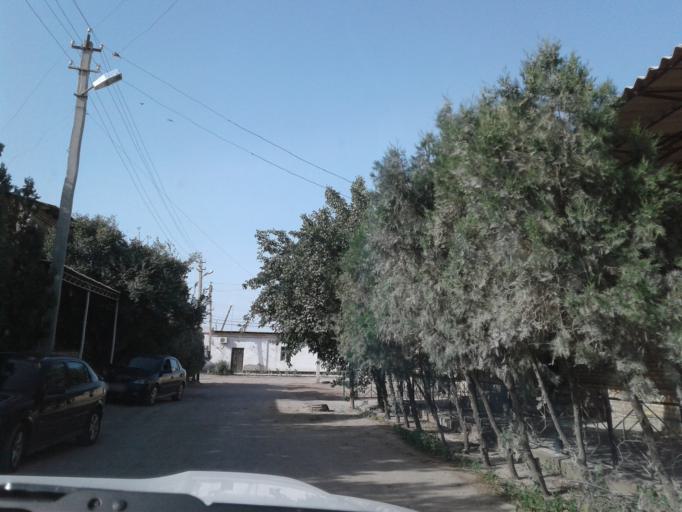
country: TM
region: Dasoguz
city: Dasoguz
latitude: 41.8480
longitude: 59.9241
